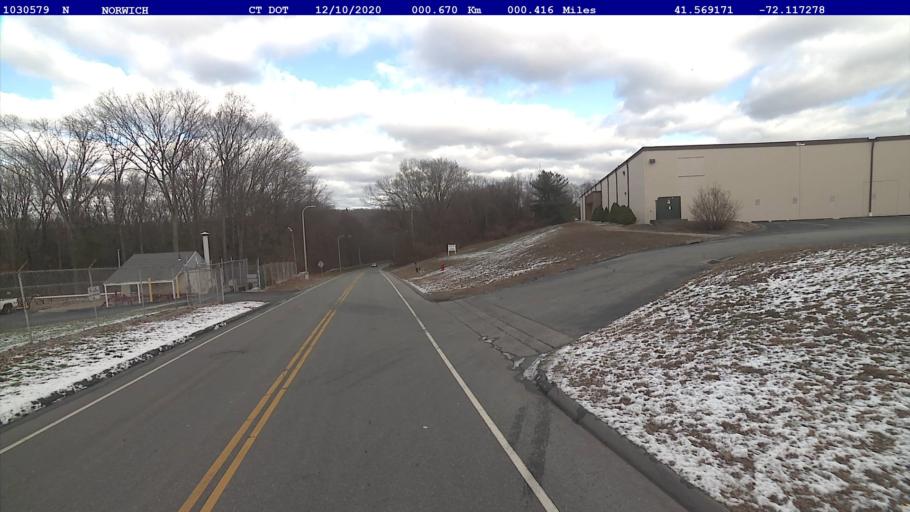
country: US
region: Connecticut
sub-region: New London County
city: Baltic
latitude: 41.5692
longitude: -72.1172
